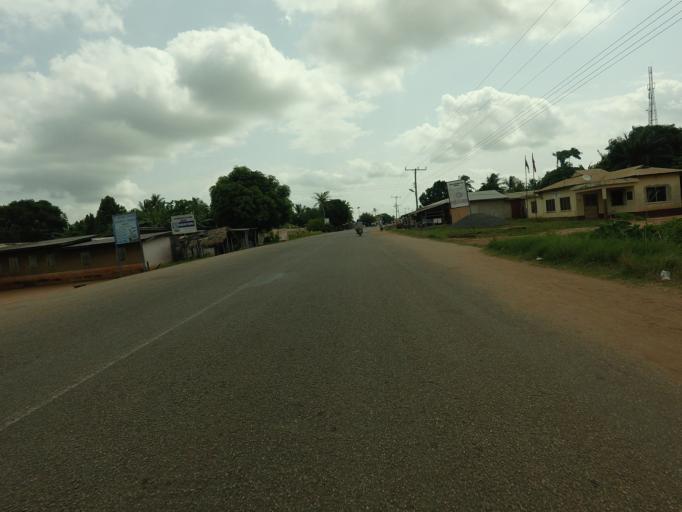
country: TG
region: Maritime
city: Lome
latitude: 6.2218
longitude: 1.0356
